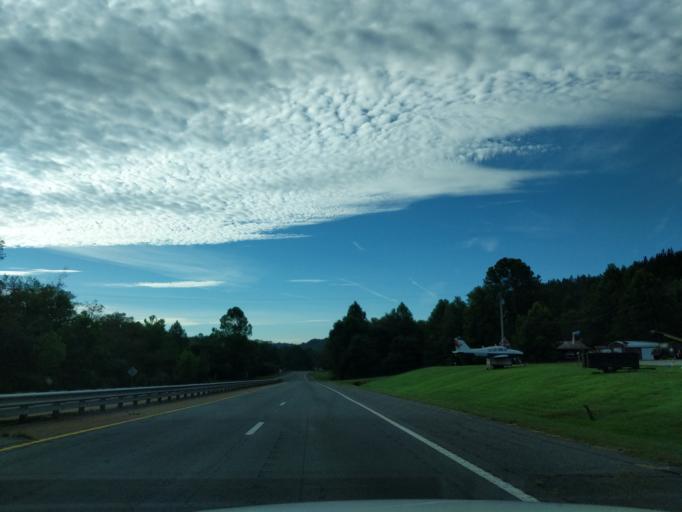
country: US
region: Georgia
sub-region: Fannin County
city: McCaysville
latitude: 35.0010
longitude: -84.3857
